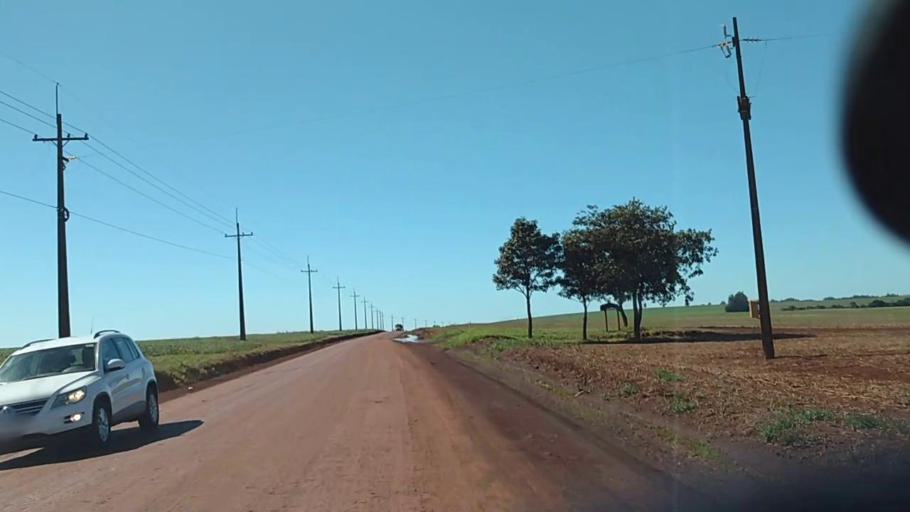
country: PY
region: Alto Parana
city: Naranjal
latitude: -25.9406
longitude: -55.2926
